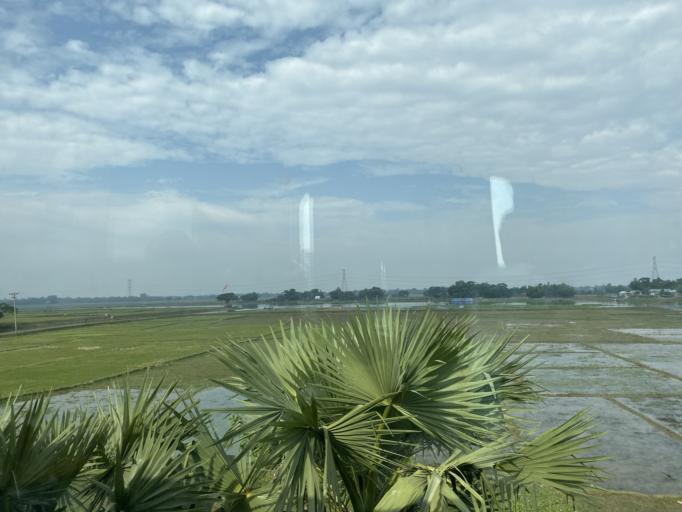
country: IN
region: Tripura
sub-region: West Tripura
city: Agartala
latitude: 23.8848
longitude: 91.2071
